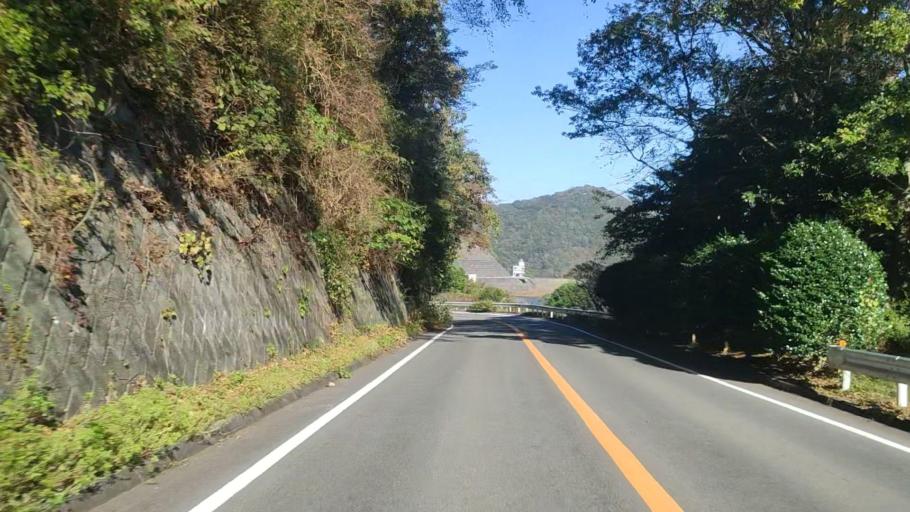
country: JP
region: Shizuoka
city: Ito
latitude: 34.9327
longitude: 139.0588
